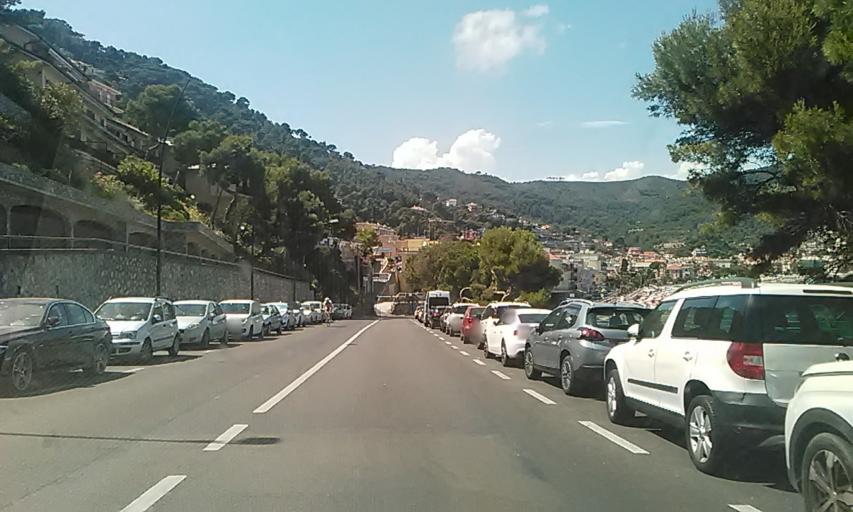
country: IT
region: Liguria
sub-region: Provincia di Savona
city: Laigueglia
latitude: 43.9690
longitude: 8.1621
